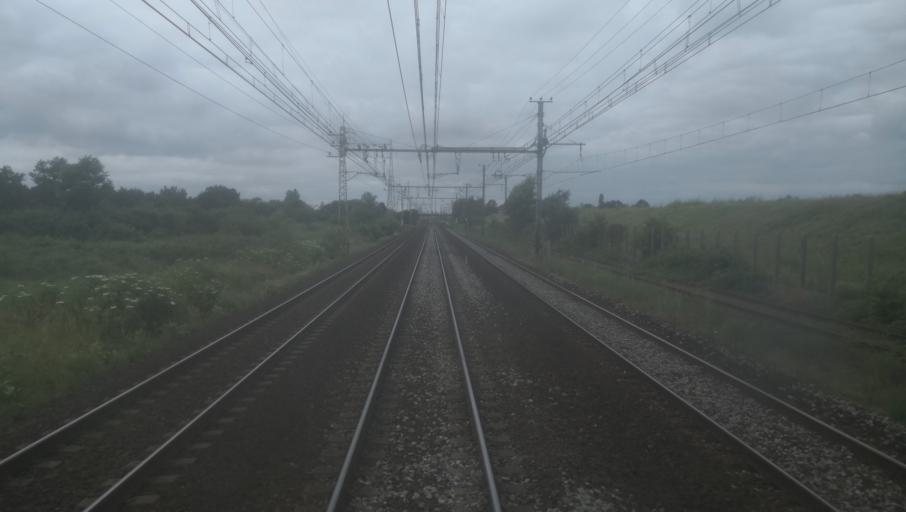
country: FR
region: Midi-Pyrenees
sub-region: Departement de la Haute-Garonne
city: Fenouillet
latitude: 43.6798
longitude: 1.4041
